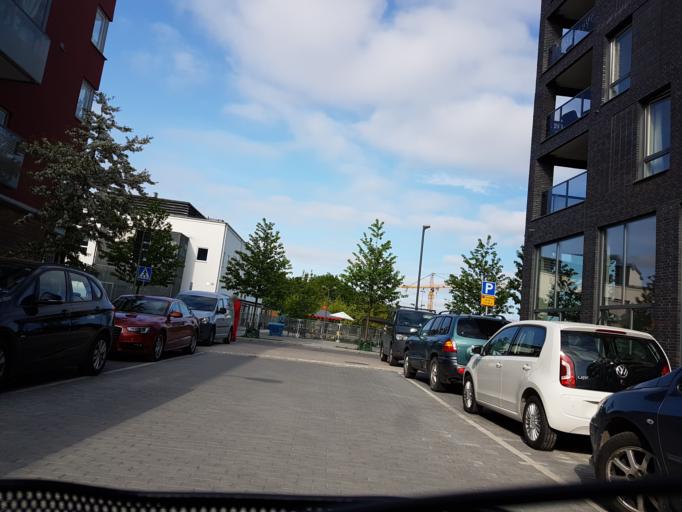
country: SE
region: Stockholm
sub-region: Stockholms Kommun
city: Bromma
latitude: 59.3630
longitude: 17.9458
